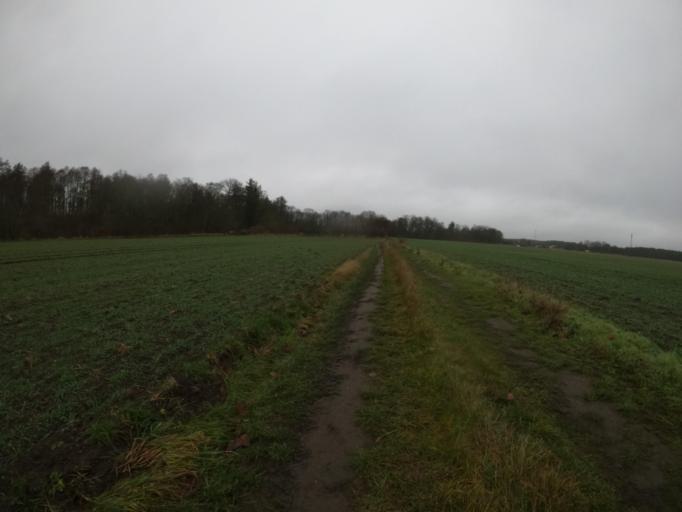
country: PL
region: West Pomeranian Voivodeship
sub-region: Powiat mysliborski
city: Debno
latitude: 52.7794
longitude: 14.7619
